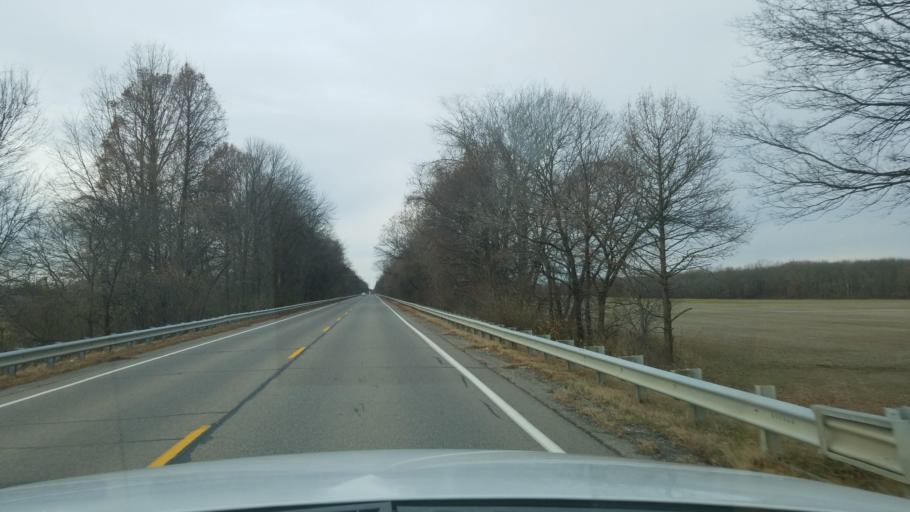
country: US
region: Indiana
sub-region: Posey County
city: Mount Vernon
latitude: 37.9291
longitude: -87.9645
